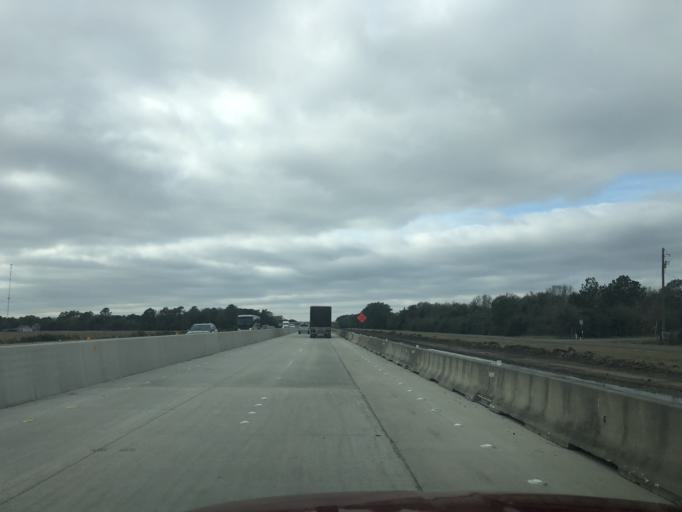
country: US
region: Texas
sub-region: Chambers County
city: Winnie
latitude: 29.8693
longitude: -94.3450
